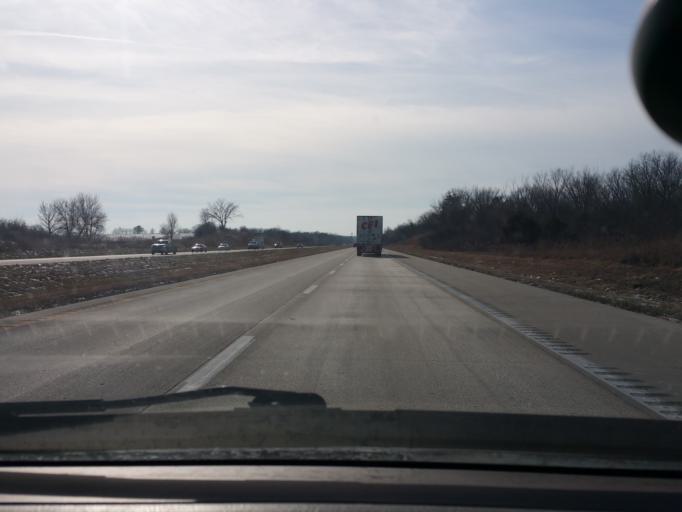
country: US
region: Missouri
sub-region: Clay County
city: Kearney
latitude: 39.4045
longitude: -94.3528
